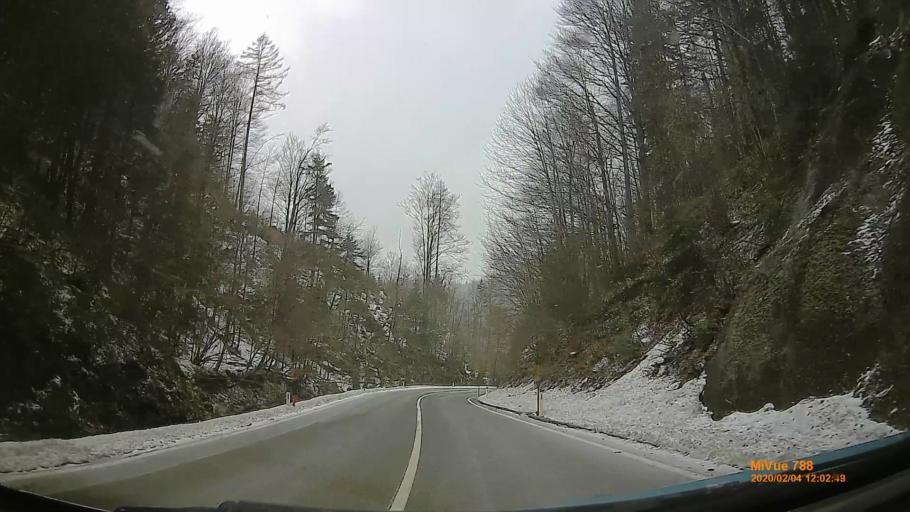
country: AT
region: Styria
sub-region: Politischer Bezirk Bruck-Muerzzuschlag
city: Muerzsteg
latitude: 47.7713
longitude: 15.4582
